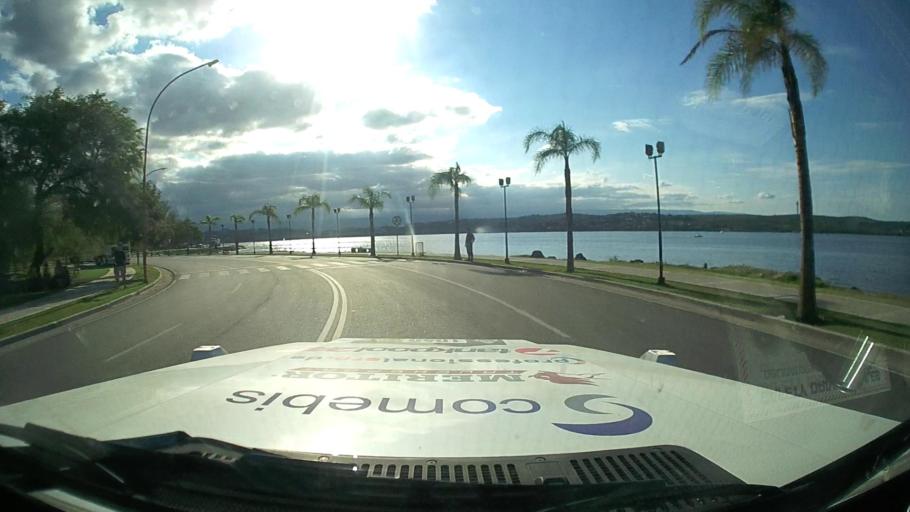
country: AR
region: Cordoba
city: Villa Carlos Paz
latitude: -31.3959
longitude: -64.4754
